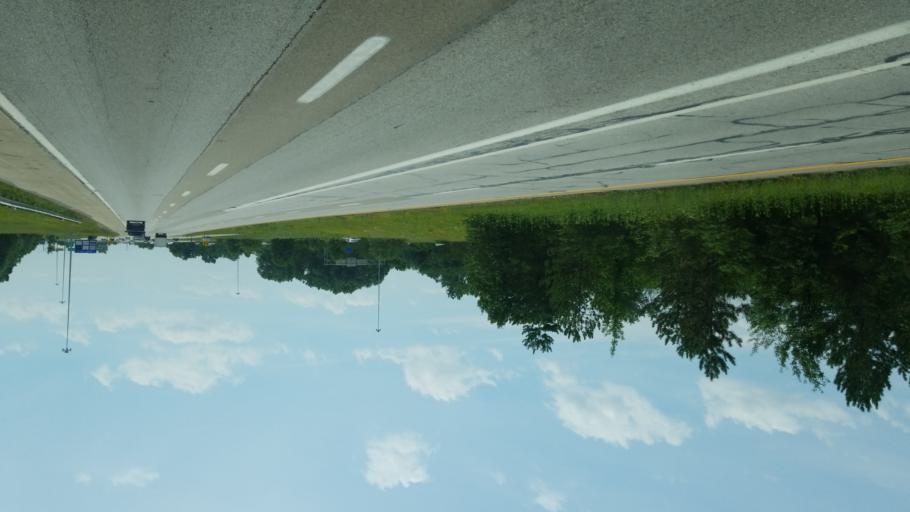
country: US
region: Ohio
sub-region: Franklin County
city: Gahanna
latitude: 40.0122
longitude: -82.9073
